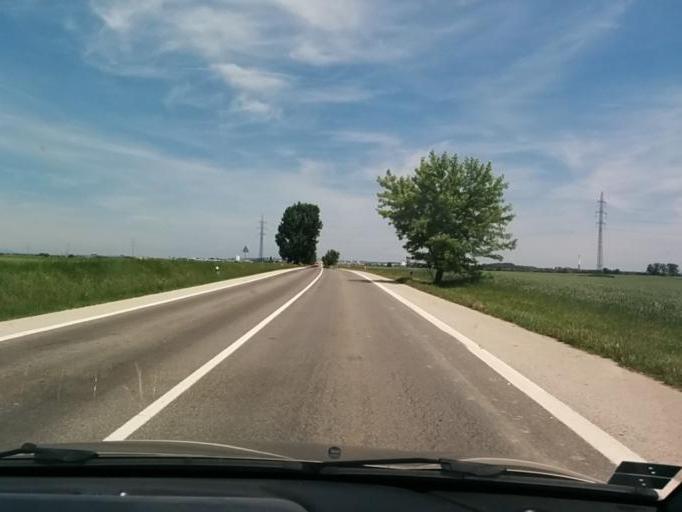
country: SK
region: Trnavsky
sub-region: Okres Galanta
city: Galanta
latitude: 48.2480
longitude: 17.7051
